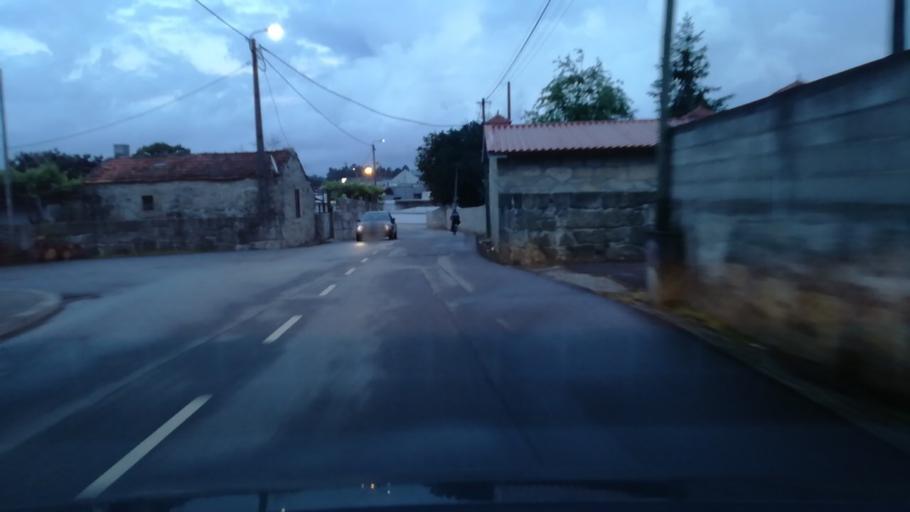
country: PT
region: Porto
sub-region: Maia
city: Maia
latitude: 41.2504
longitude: -8.6244
